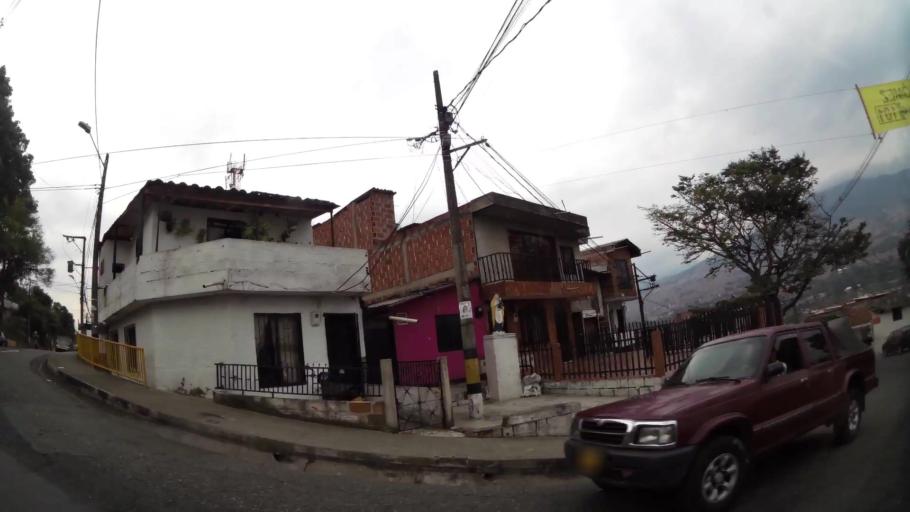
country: CO
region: Antioquia
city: Bello
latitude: 6.2959
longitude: -75.5543
